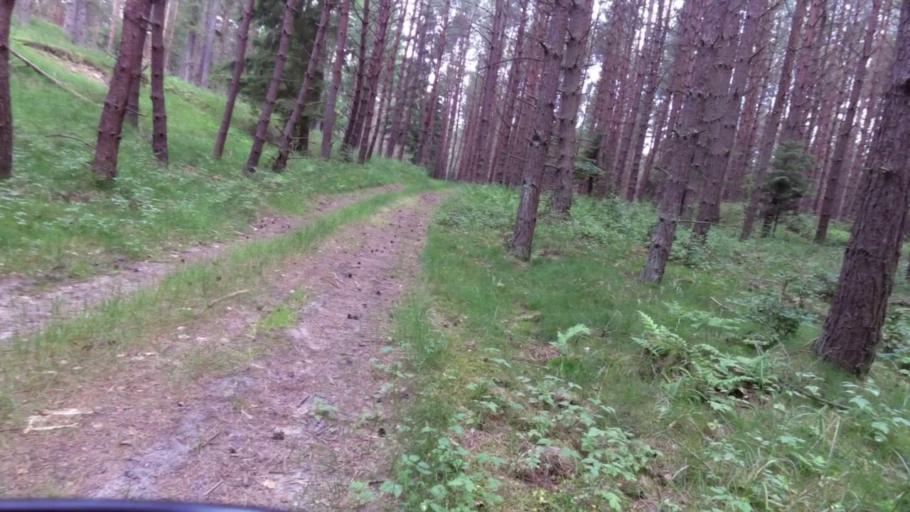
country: PL
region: West Pomeranian Voivodeship
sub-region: Powiat kamienski
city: Miedzyzdroje
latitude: 53.8740
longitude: 14.5008
